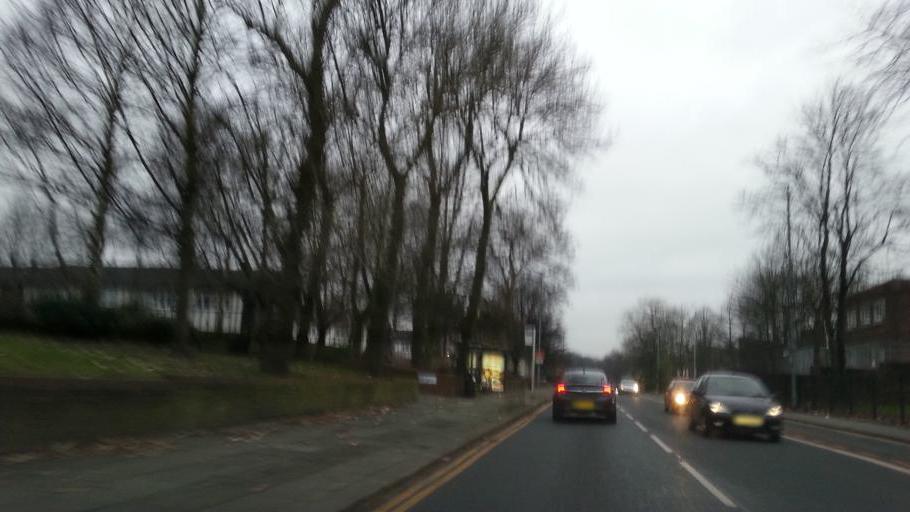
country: GB
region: England
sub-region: Manchester
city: Crumpsall
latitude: 53.5043
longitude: -2.2599
